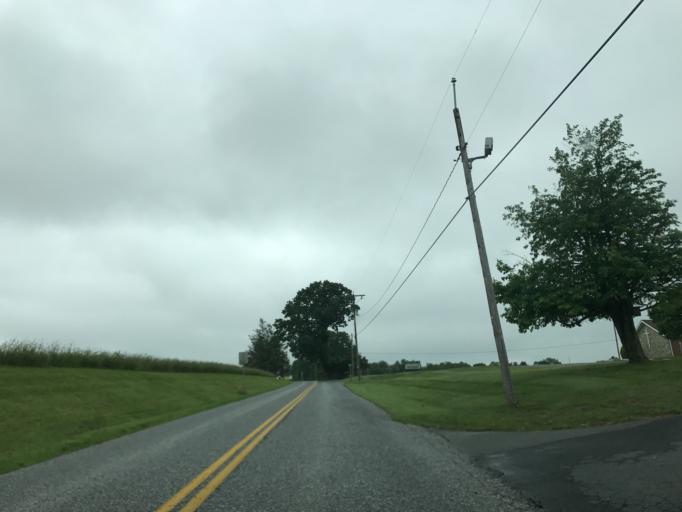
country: US
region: Pennsylvania
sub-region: York County
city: Susquehanna Trails
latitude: 39.7166
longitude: -76.4520
